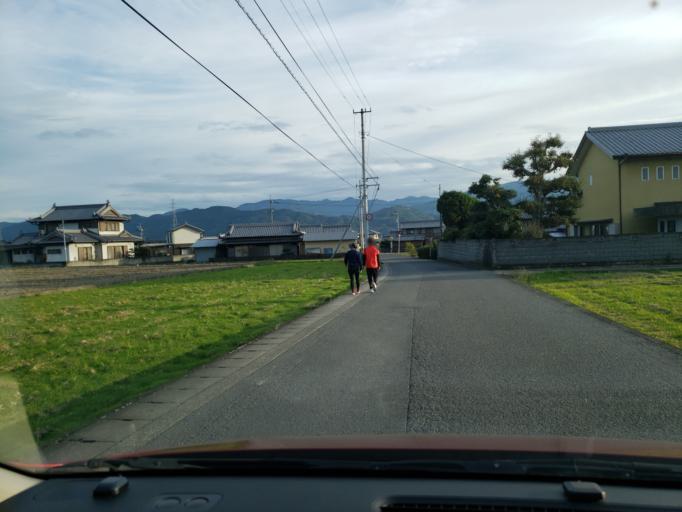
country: JP
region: Tokushima
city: Wakimachi
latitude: 34.0822
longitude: 134.2276
